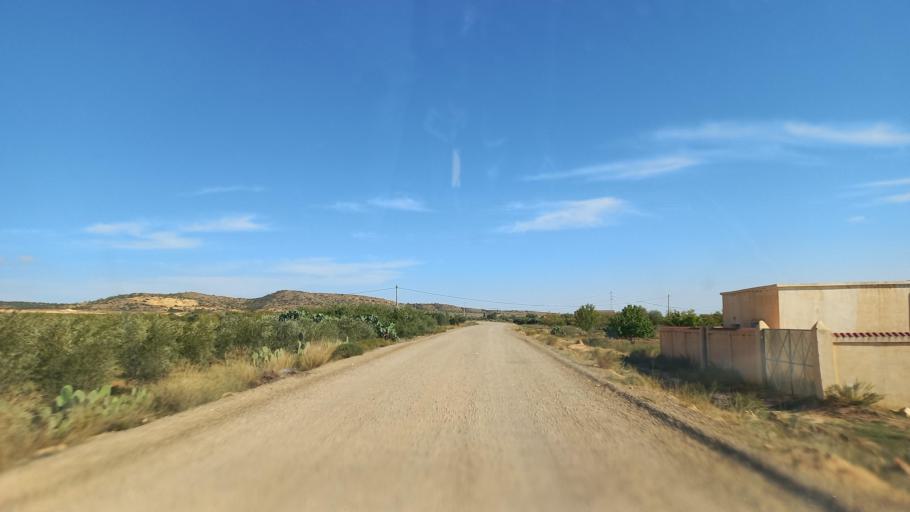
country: TN
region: Al Qasrayn
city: Sbiba
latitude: 35.2952
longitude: 9.1063
